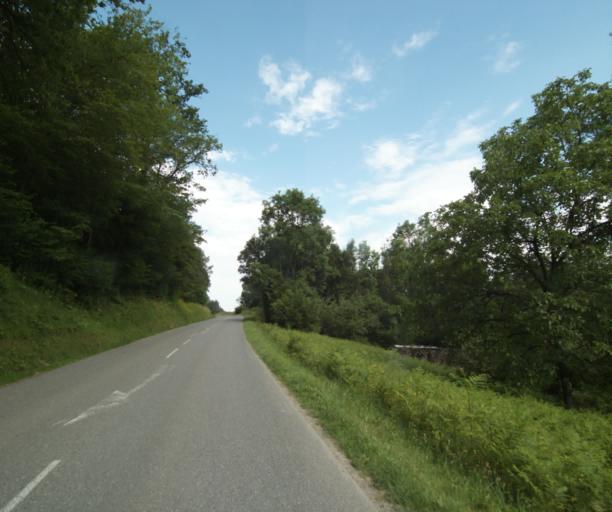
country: FR
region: Rhone-Alpes
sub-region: Departement de la Haute-Savoie
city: Allinges
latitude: 46.3356
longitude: 6.4747
